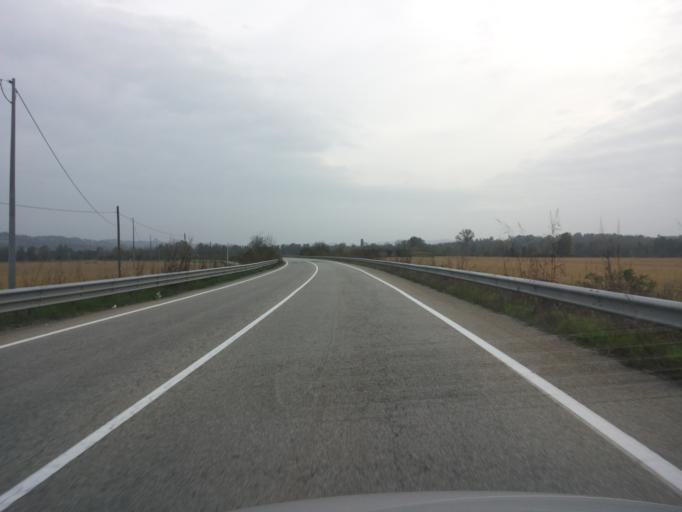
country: IT
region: Piedmont
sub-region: Provincia di Alessandria
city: Pontestura
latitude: 45.1592
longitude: 8.3318
